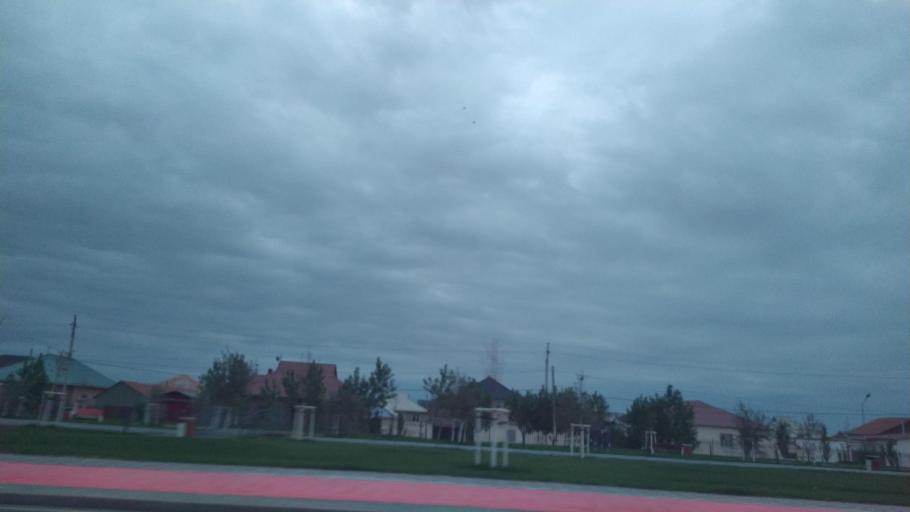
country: KZ
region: Ongtustik Qazaqstan
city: Turkestan
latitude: 43.2802
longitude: 68.3212
